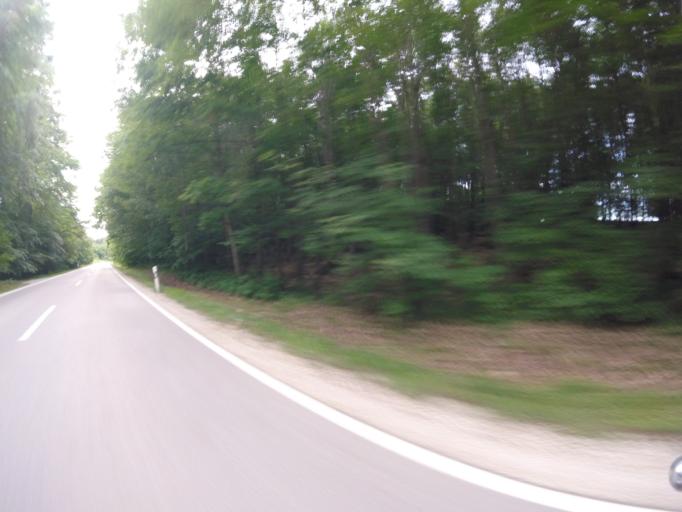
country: DE
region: Bavaria
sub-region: Upper Bavaria
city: Paunzhausen
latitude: 48.4803
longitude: 11.5469
